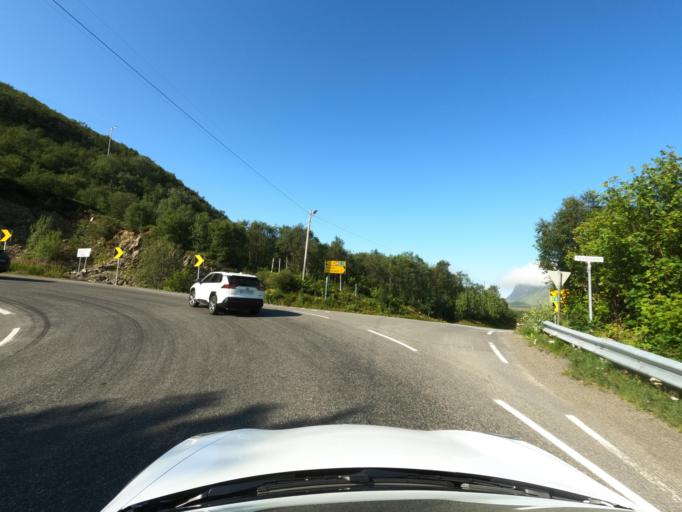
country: NO
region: Nordland
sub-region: Vestvagoy
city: Evjen
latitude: 68.2929
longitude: 13.8647
